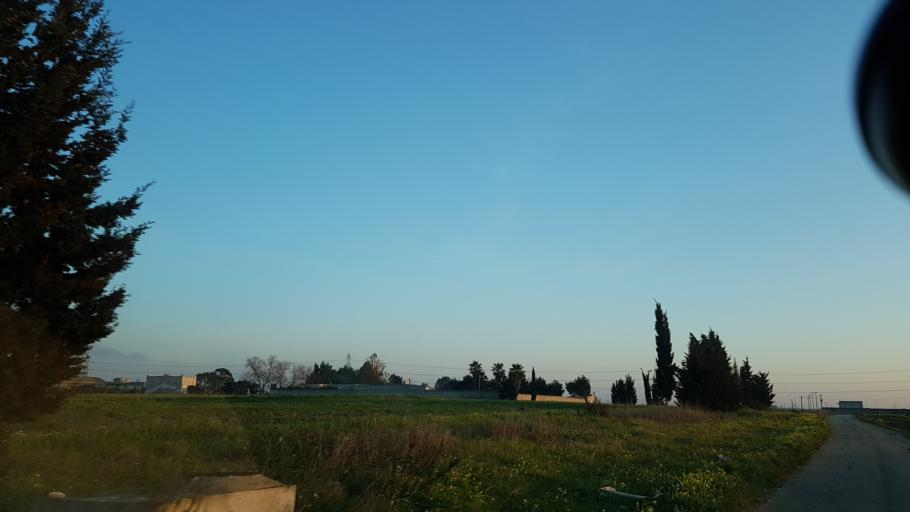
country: IT
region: Apulia
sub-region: Provincia di Brindisi
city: La Rosa
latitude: 40.5993
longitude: 17.9515
